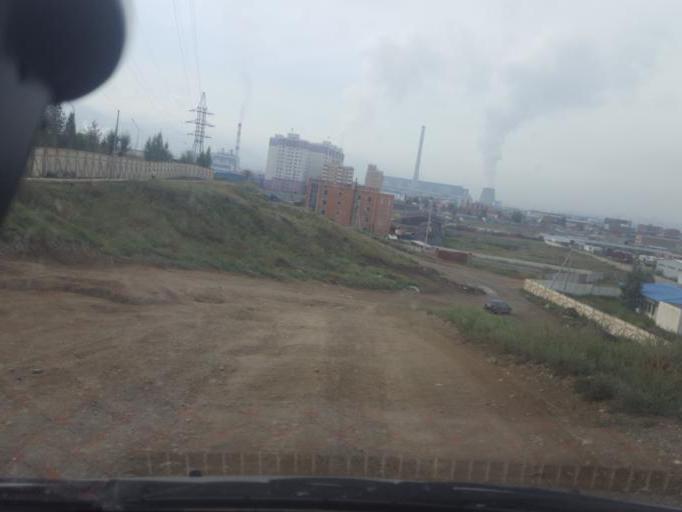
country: MN
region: Ulaanbaatar
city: Ulaanbaatar
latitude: 47.9165
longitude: 106.8006
